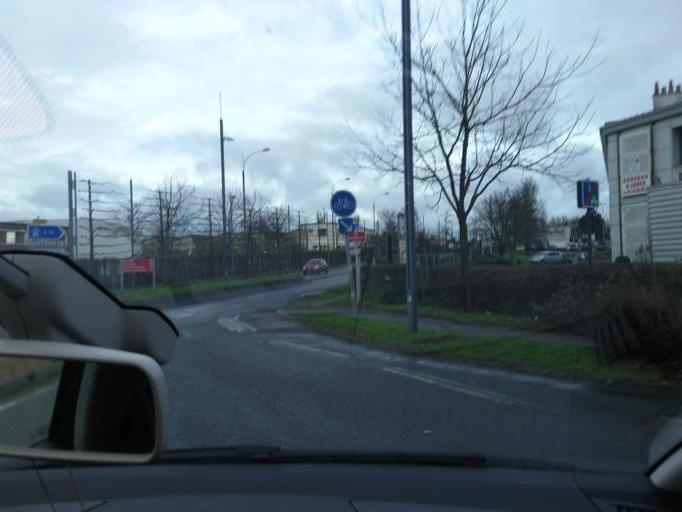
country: FR
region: Picardie
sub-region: Departement de la Somme
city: Amiens
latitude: 49.9320
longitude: 2.2766
